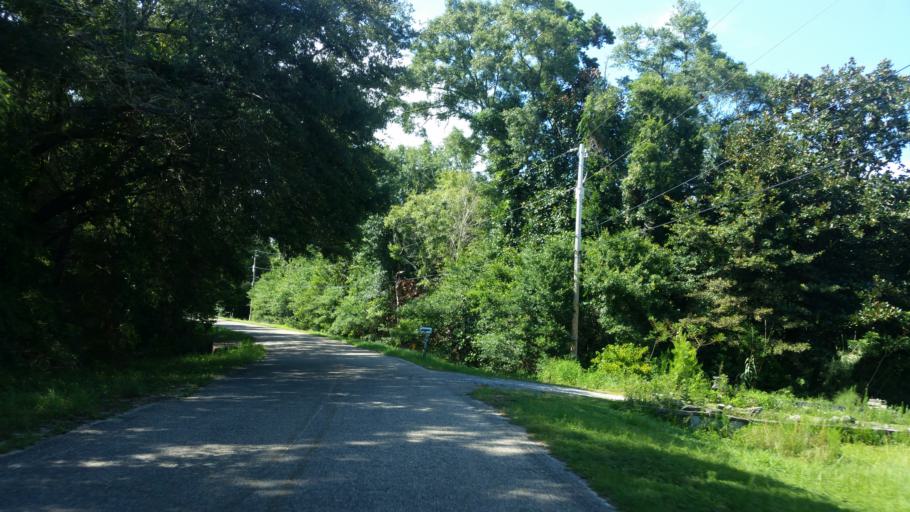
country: US
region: Florida
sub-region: Santa Rosa County
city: Pace
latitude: 30.5794
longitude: -87.1528
